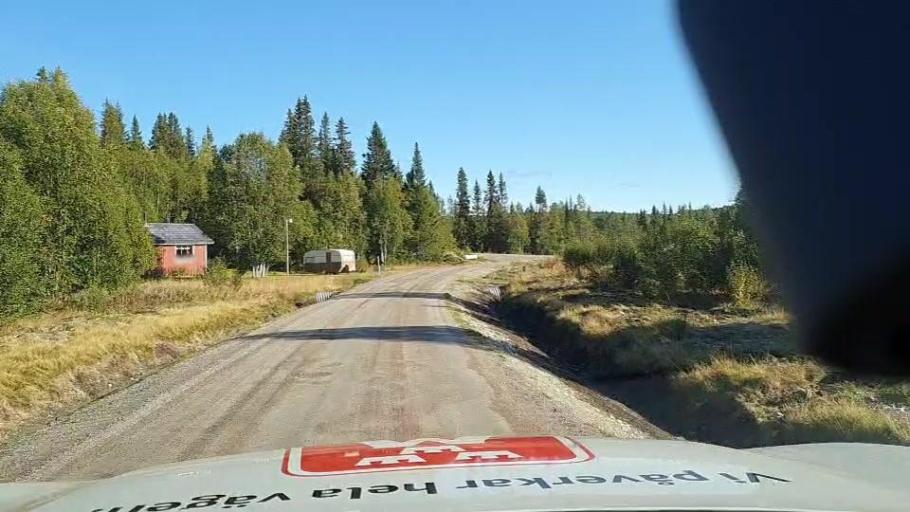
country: SE
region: Jaemtland
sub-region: Stroemsunds Kommun
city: Stroemsund
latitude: 64.5074
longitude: 15.1485
